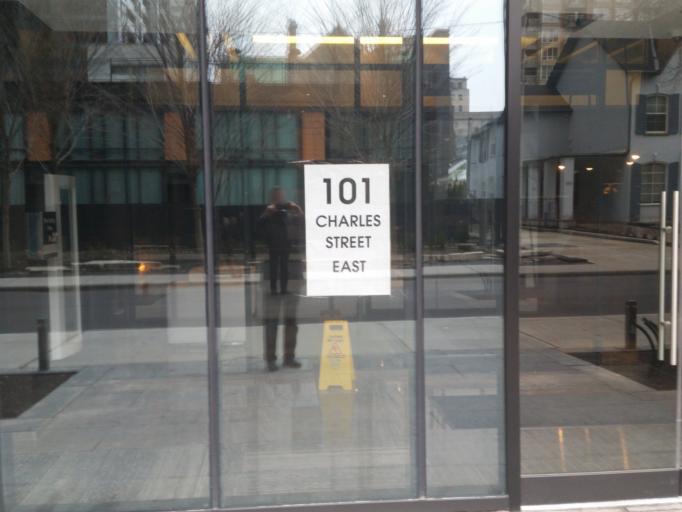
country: CA
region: Ontario
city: Toronto
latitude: 43.6698
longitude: -79.3802
